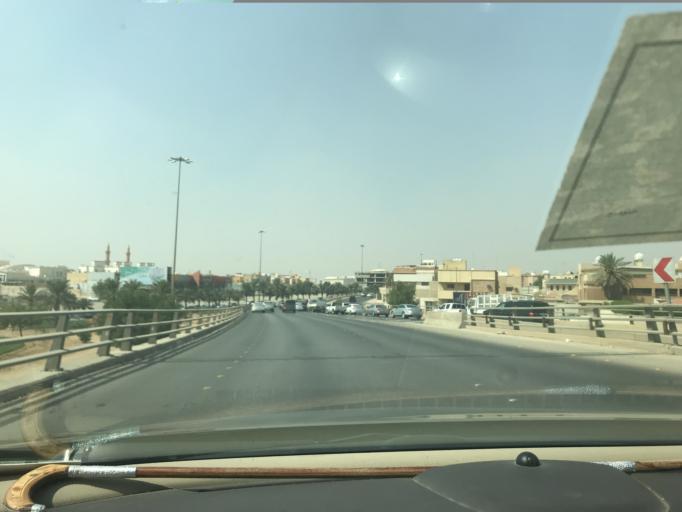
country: SA
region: Ar Riyad
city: Riyadh
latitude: 24.7164
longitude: 46.7622
